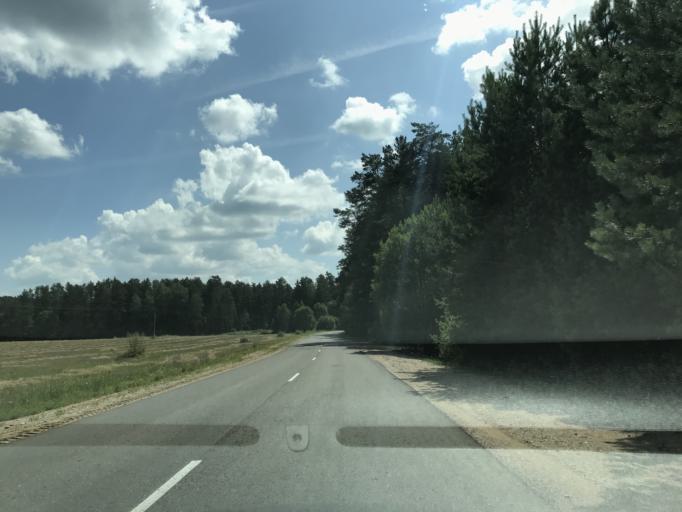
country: BY
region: Minsk
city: Rakaw
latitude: 54.0055
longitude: 26.9830
